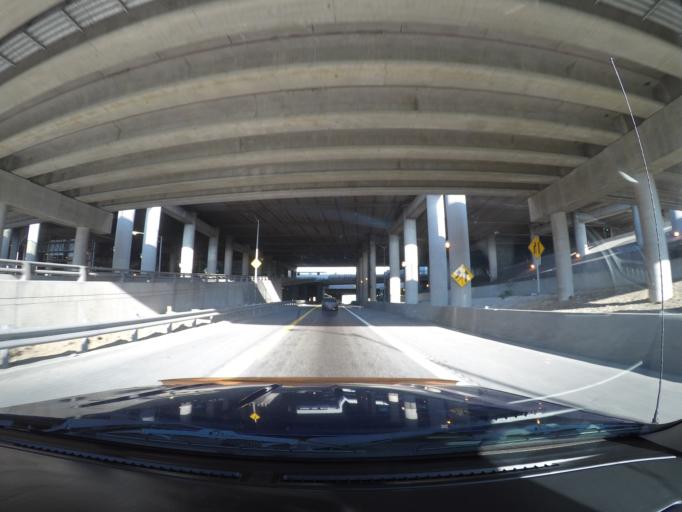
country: US
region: Missouri
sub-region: Jackson County
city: Kansas City
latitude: 39.0962
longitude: -94.5887
